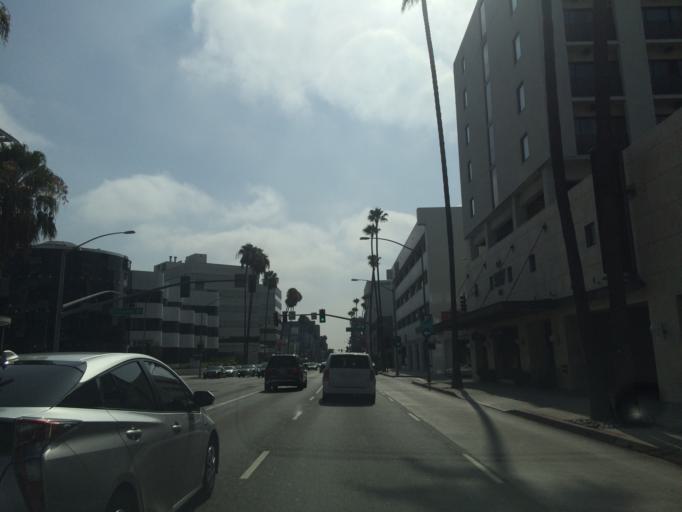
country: US
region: California
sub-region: Los Angeles County
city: Beverly Hills
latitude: 34.0670
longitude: -118.3965
